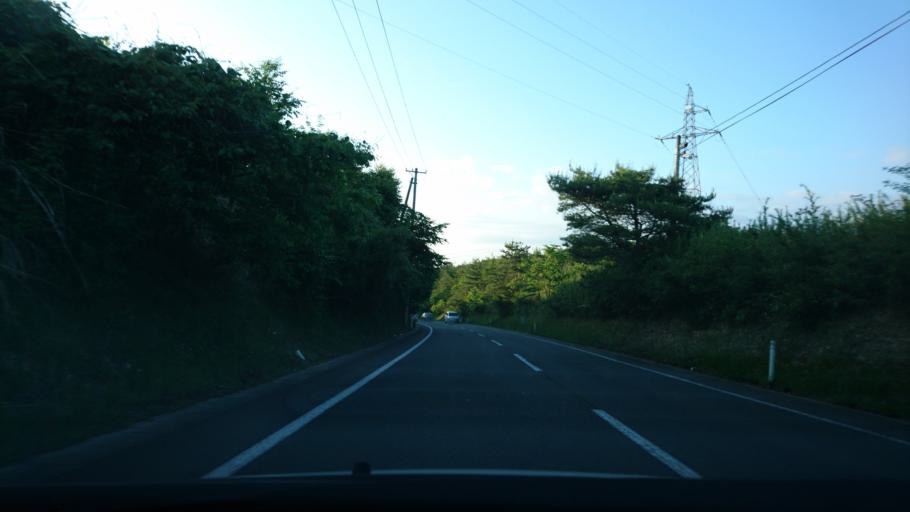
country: JP
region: Iwate
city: Ichinoseki
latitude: 38.8818
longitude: 141.1586
